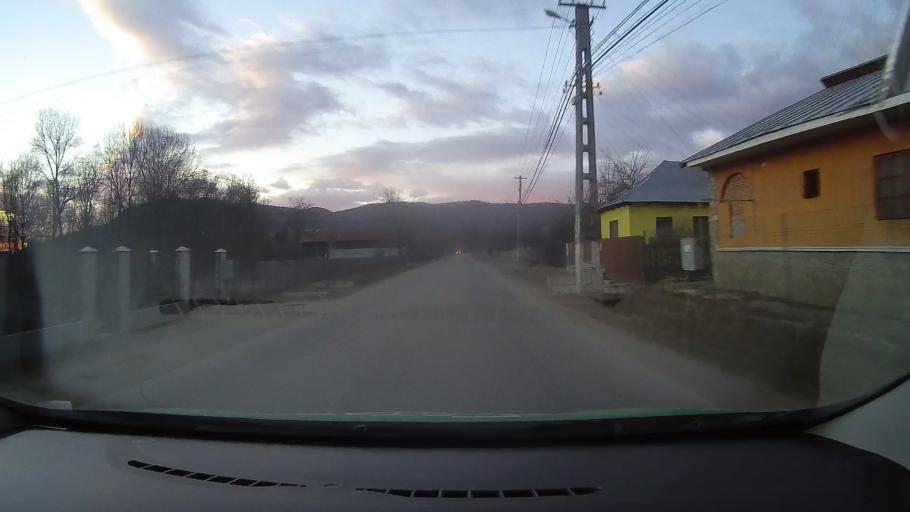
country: RO
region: Dambovita
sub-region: Comuna Valea Lunga
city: Valea Lunga-Cricov
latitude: 45.0675
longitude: 25.5829
